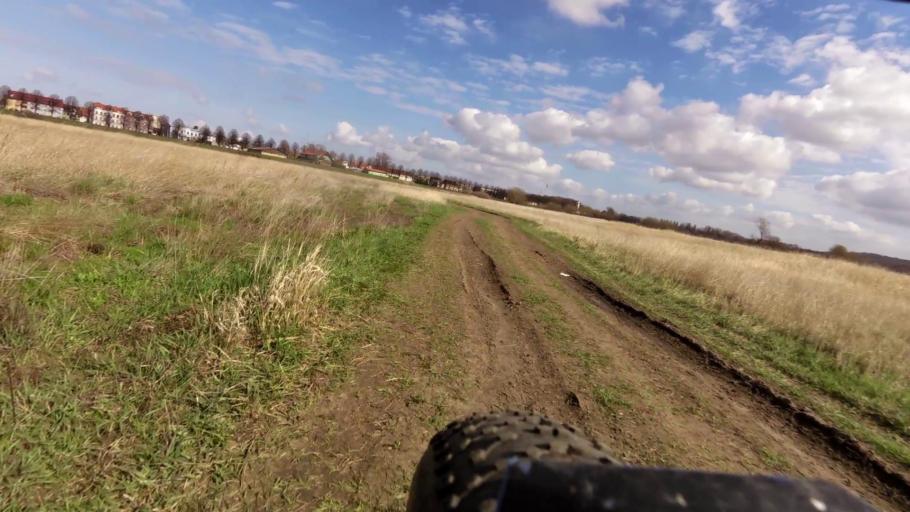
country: PL
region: Lubusz
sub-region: Powiat slubicki
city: Slubice
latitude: 52.3469
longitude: 14.5741
